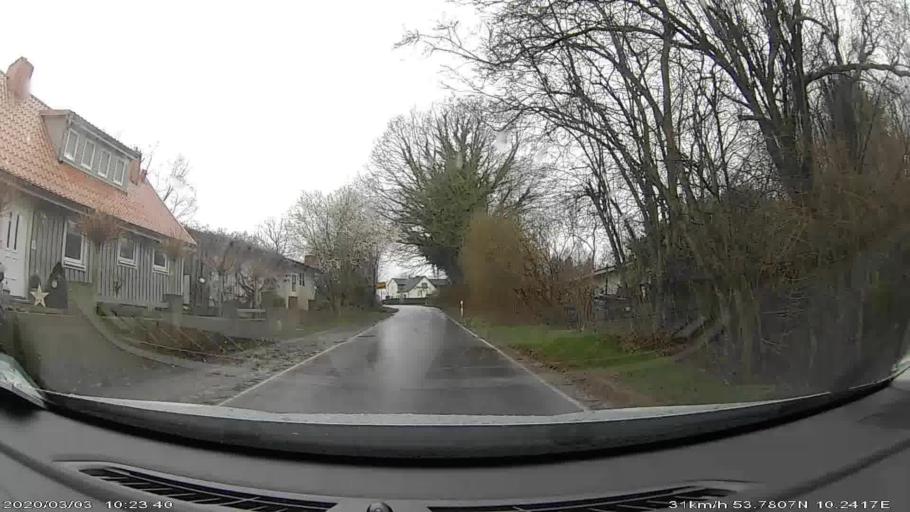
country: DE
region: Schleswig-Holstein
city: Sulfeld
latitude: 53.7798
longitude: 10.2374
